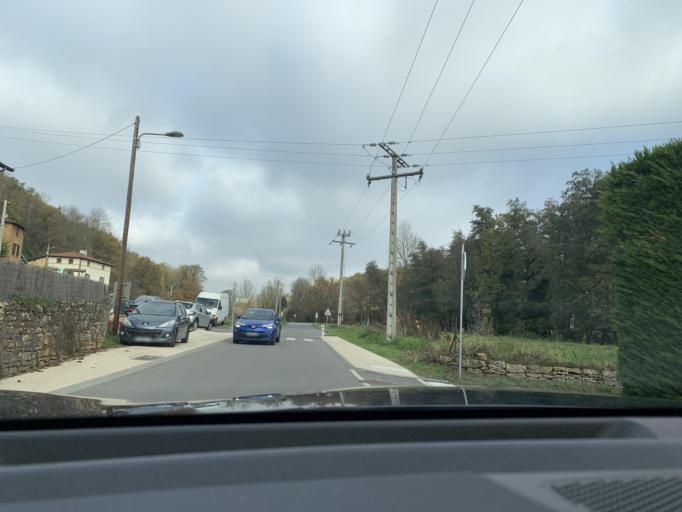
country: FR
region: Rhone-Alpes
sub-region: Departement du Rhone
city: Charnay
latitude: 45.8787
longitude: 4.6472
